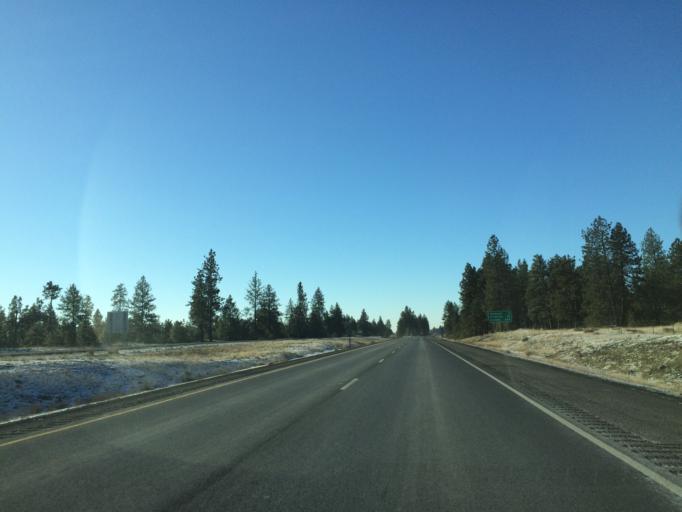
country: US
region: Washington
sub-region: Spokane County
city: Medical Lake
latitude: 47.4286
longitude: -117.8003
